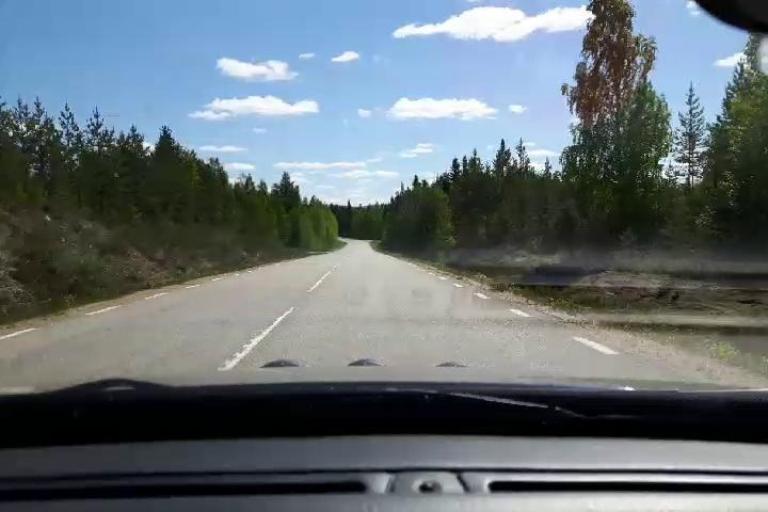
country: SE
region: Gaevleborg
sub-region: Ljusdals Kommun
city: Farila
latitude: 61.9989
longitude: 15.2417
